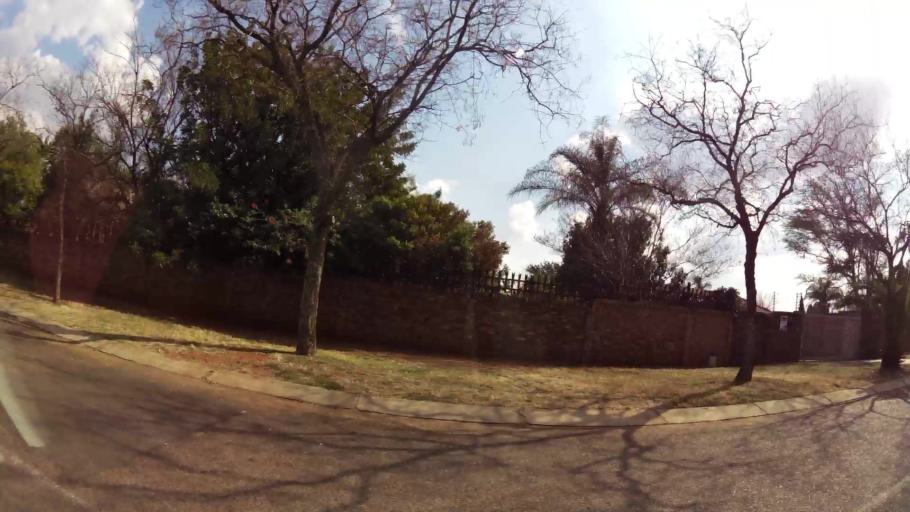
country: ZA
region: Gauteng
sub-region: City of Tshwane Metropolitan Municipality
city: Centurion
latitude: -25.8321
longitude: 28.2382
